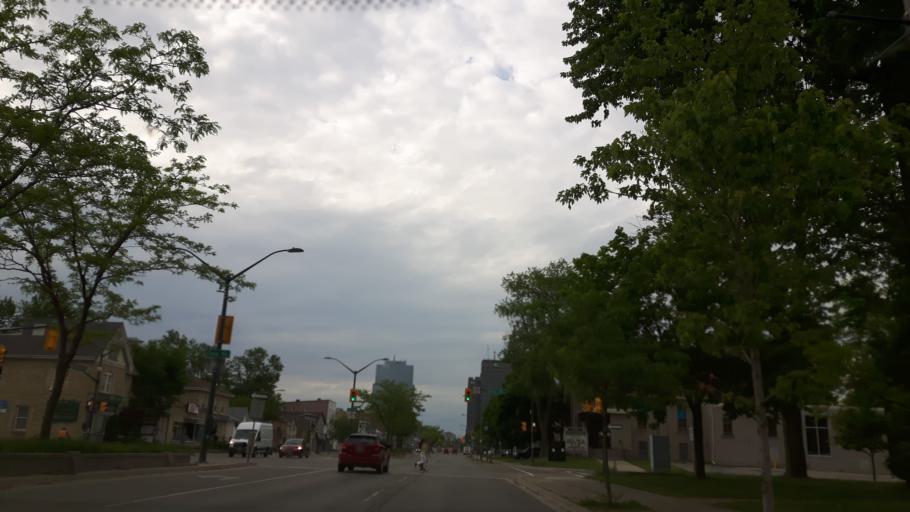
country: CA
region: Ontario
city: London
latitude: 42.9774
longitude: -81.2414
